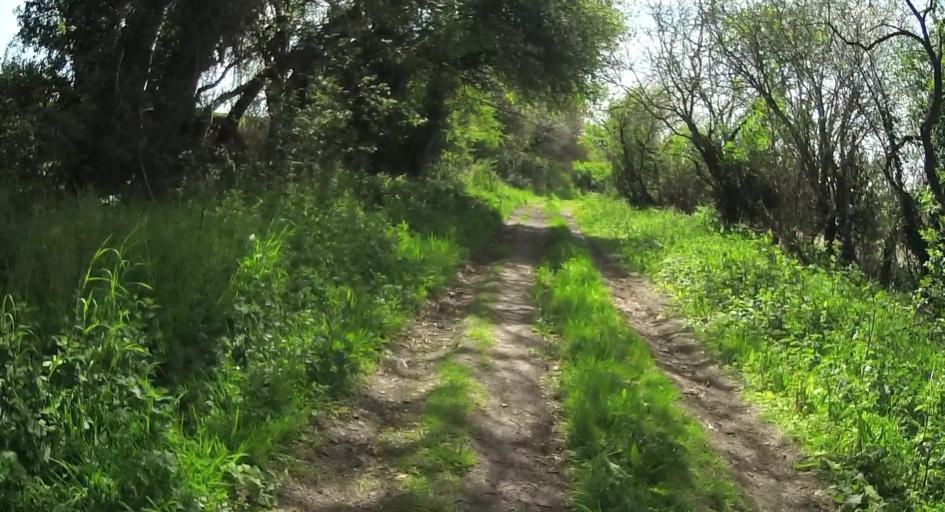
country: GB
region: England
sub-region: Hampshire
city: Chandlers Ford
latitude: 51.0944
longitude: -1.4144
